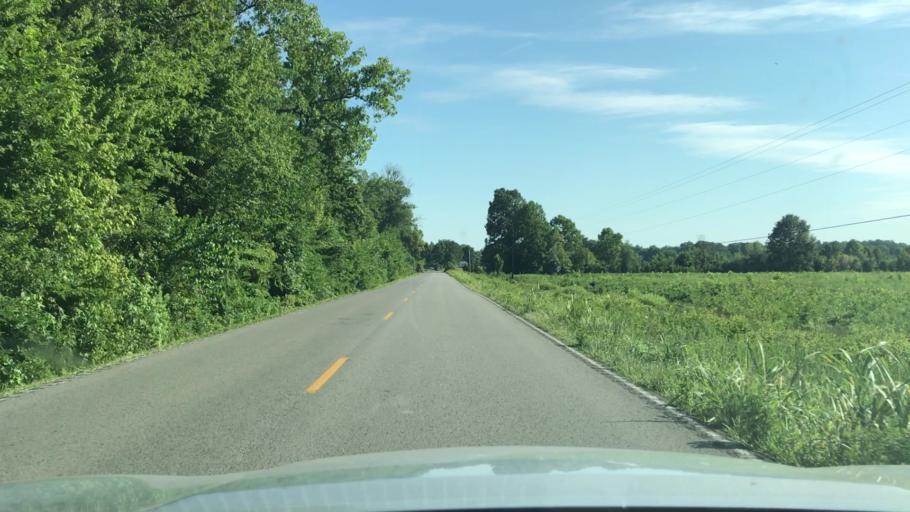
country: US
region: Kentucky
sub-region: Muhlenberg County
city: Greenville
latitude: 37.1414
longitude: -87.1425
